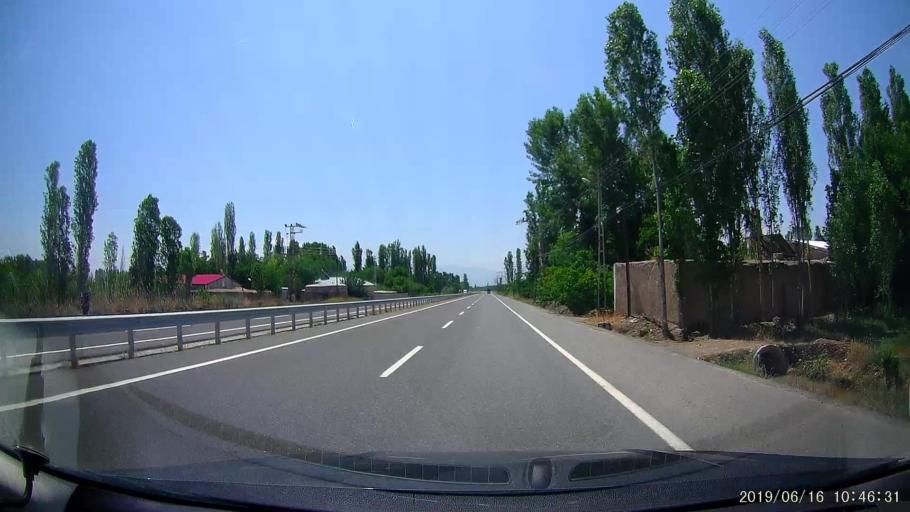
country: AM
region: Armavir
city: Shenavan
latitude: 40.0210
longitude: 43.8798
